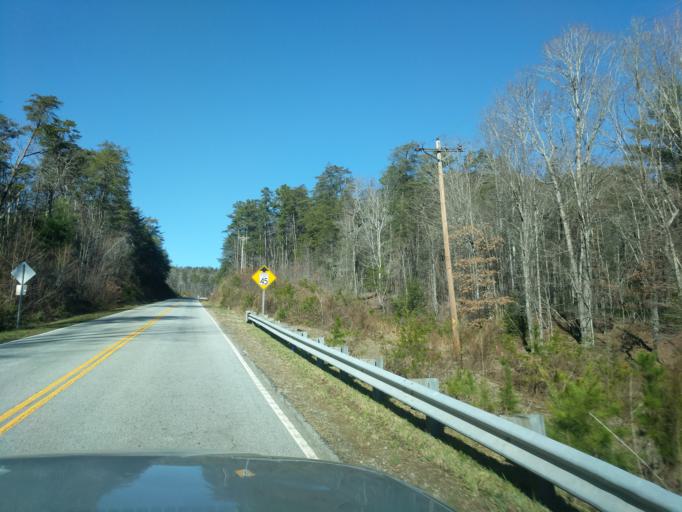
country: US
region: South Carolina
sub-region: Oconee County
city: Westminster
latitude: 34.7599
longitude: -83.2480
